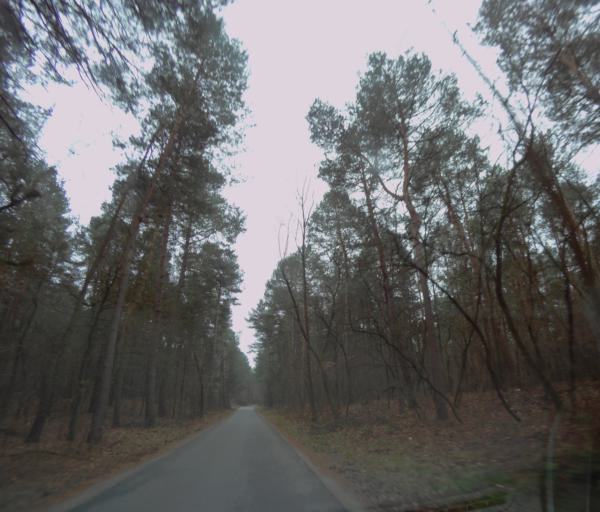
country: PL
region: Subcarpathian Voivodeship
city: Nowa Sarzyna
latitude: 50.3037
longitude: 22.3468
